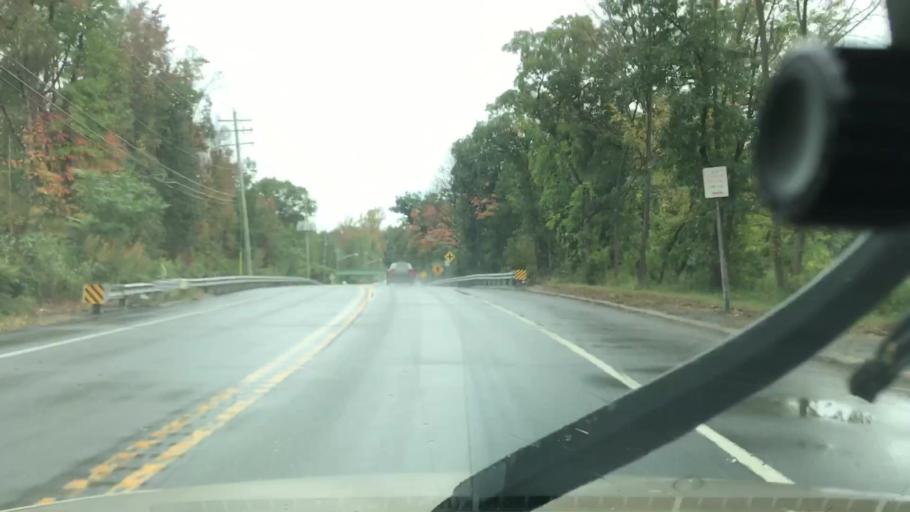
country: US
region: New Jersey
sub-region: Bergen County
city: Alpine
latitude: 40.9803
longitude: -73.9136
